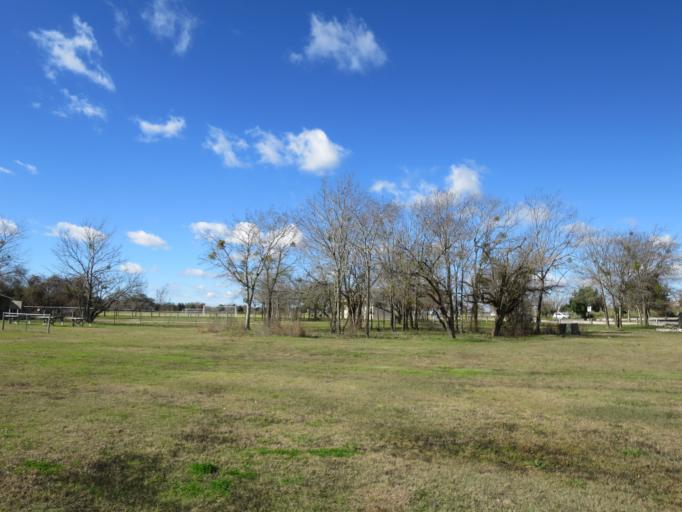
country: US
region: Texas
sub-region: Williamson County
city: Round Rock
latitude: 30.5323
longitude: -97.6288
